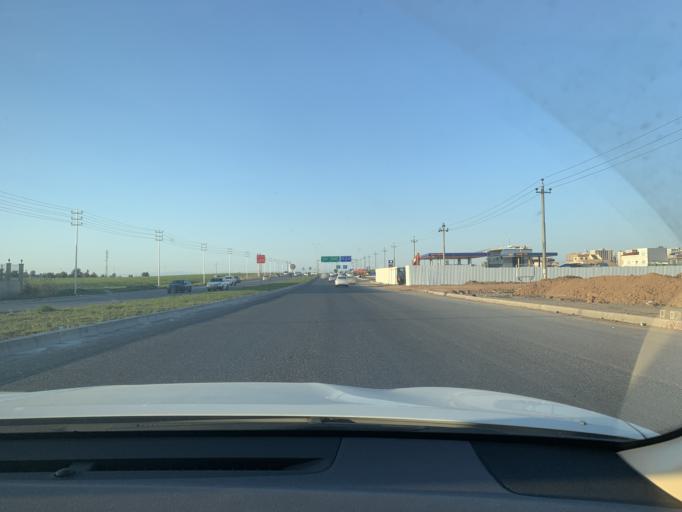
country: IQ
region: Arbil
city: Erbil
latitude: 36.2820
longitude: 44.0159
